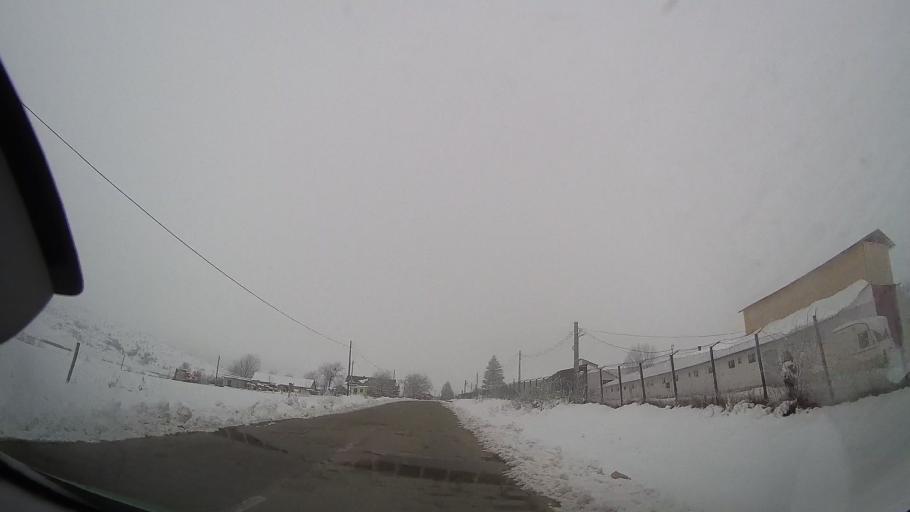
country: RO
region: Neamt
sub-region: Comuna Icusesti
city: Balusesti
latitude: 46.8566
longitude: 27.0282
